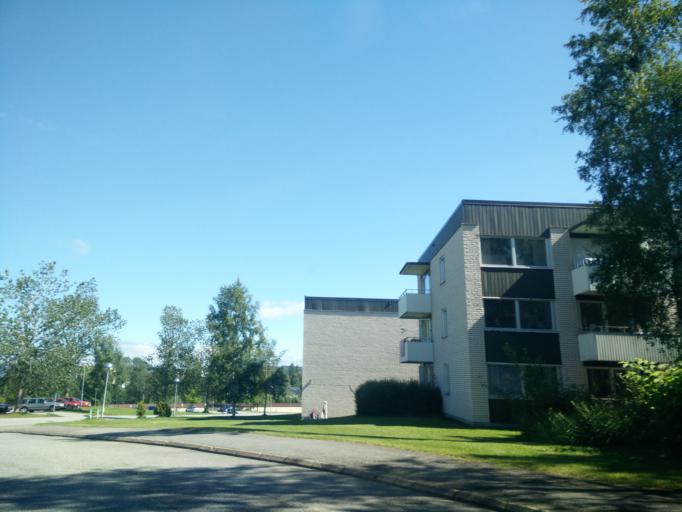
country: SE
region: Vaesternorrland
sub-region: Haernoesands Kommun
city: Haernoesand
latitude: 62.6271
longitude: 17.9119
